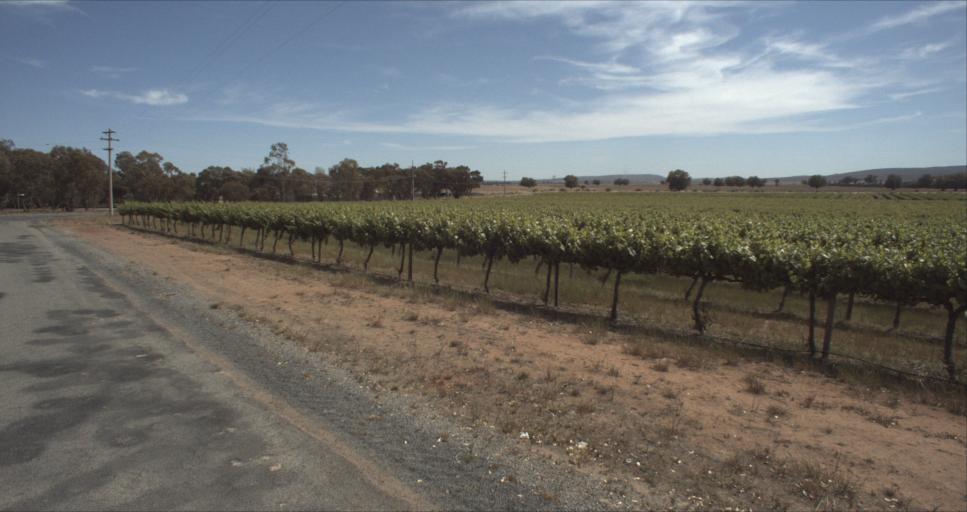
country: AU
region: New South Wales
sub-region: Leeton
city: Leeton
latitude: -34.5606
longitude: 146.4589
